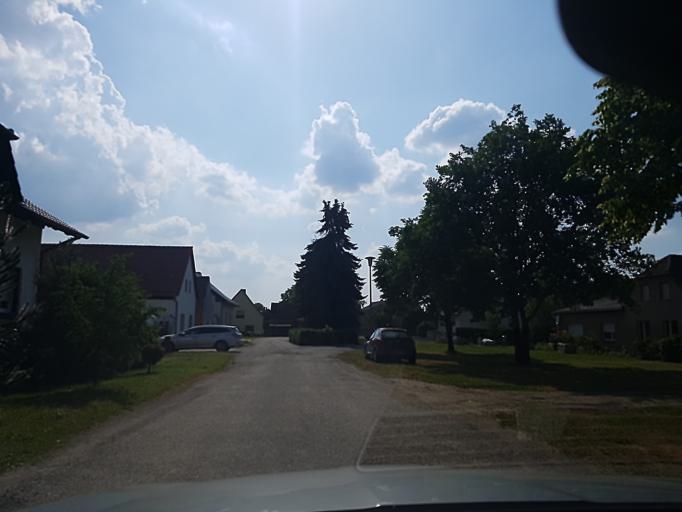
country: DE
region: Brandenburg
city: Schonborn
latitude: 51.5600
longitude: 13.4796
